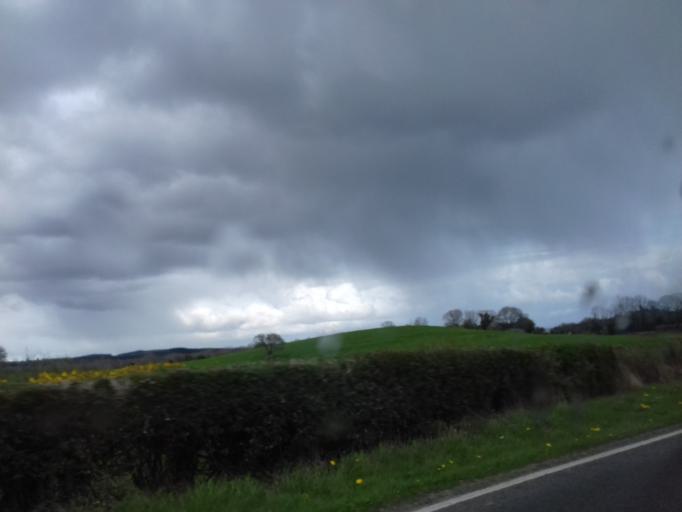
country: IE
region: Ulster
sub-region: County Donegal
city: Ballyshannon
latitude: 54.4695
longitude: -7.9812
